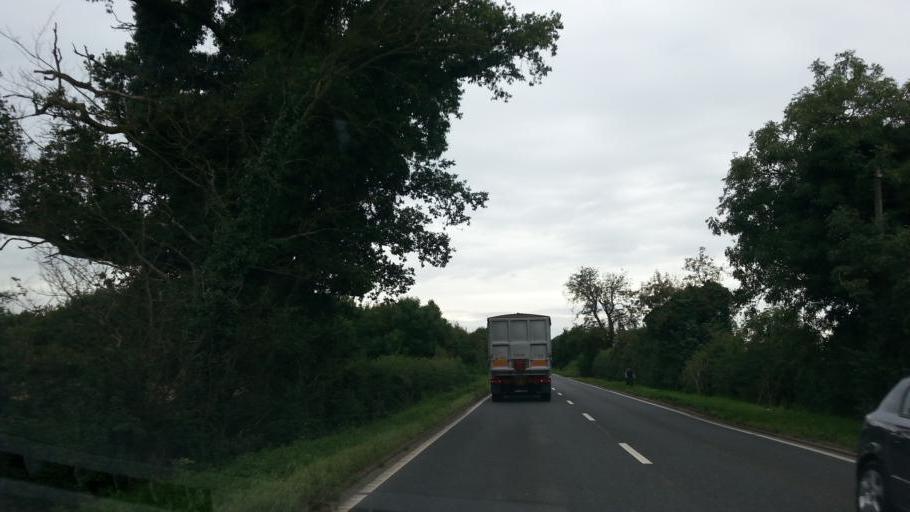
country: GB
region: England
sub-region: Peterborough
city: Thorney
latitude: 52.6192
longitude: -0.1278
